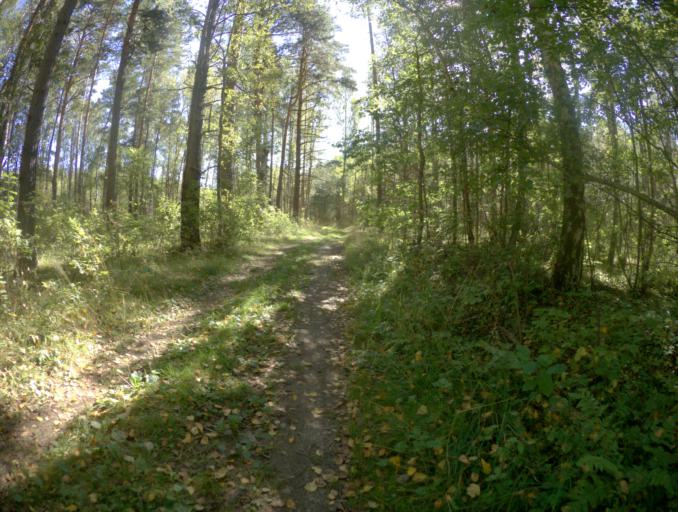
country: RU
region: Vladimir
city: Nikologory
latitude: 56.1091
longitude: 41.9189
